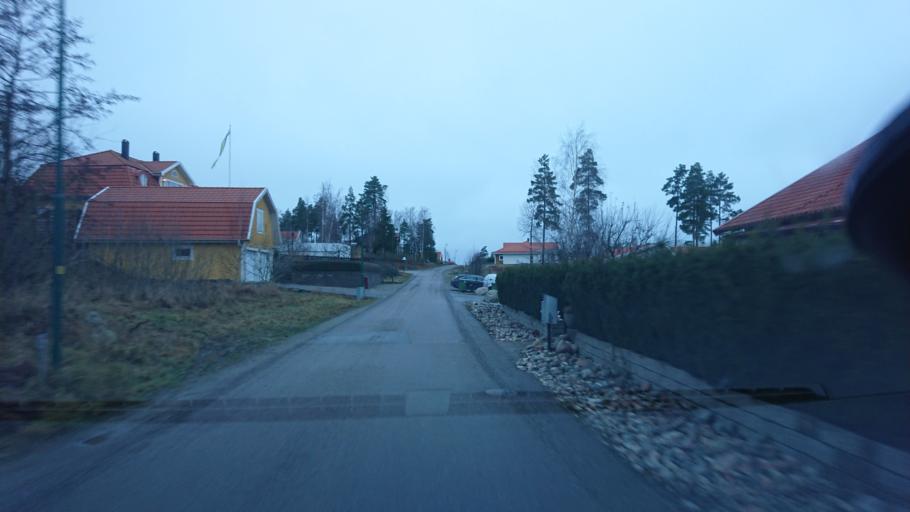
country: SE
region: Soedermanland
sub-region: Strangnas Kommun
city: Stallarholmen
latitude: 59.3639
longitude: 17.1917
